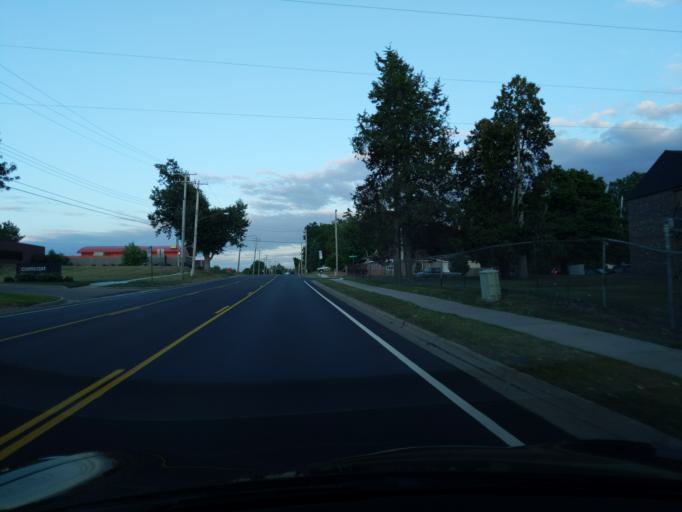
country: US
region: Michigan
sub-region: Ingham County
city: Holt
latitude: 42.6692
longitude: -84.5336
